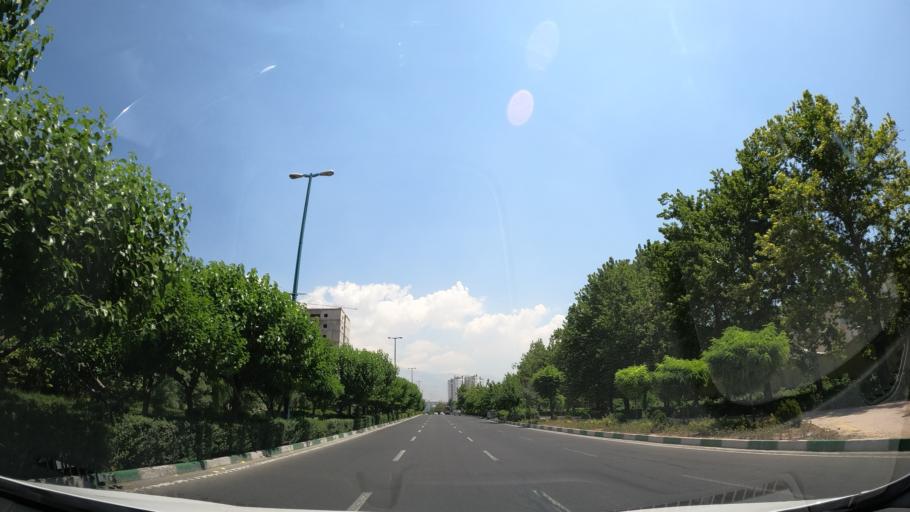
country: IR
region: Tehran
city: Tajrish
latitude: 35.7601
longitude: 51.3748
